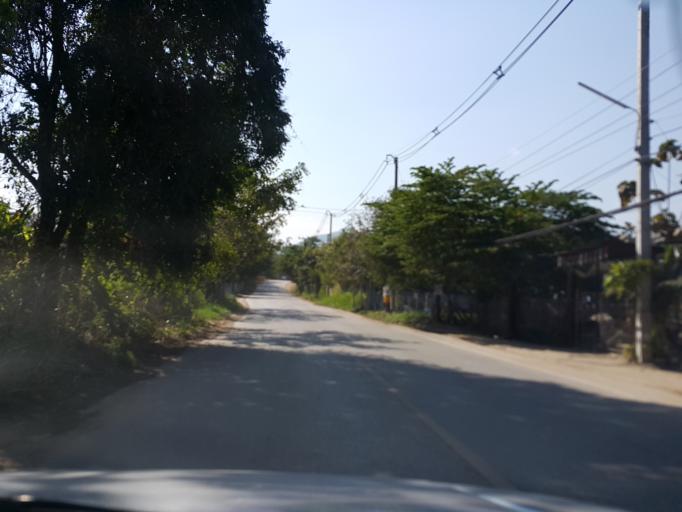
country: TH
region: Chiang Mai
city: Mae Wang
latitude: 18.6047
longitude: 98.7915
